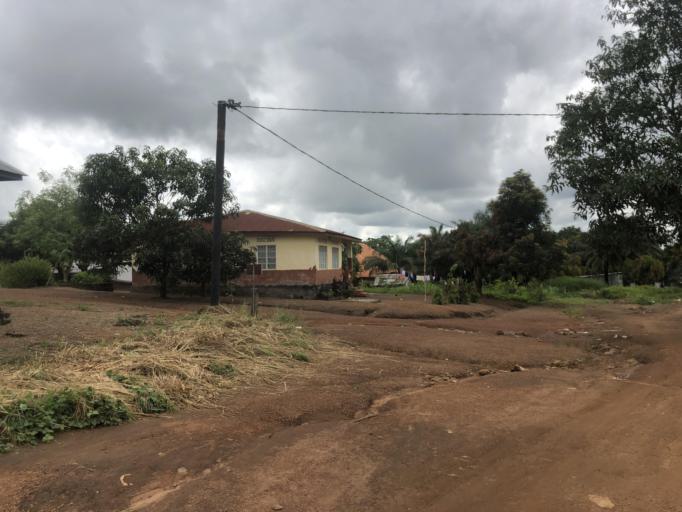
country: SL
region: Northern Province
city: Makeni
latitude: 8.9083
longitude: -12.0397
